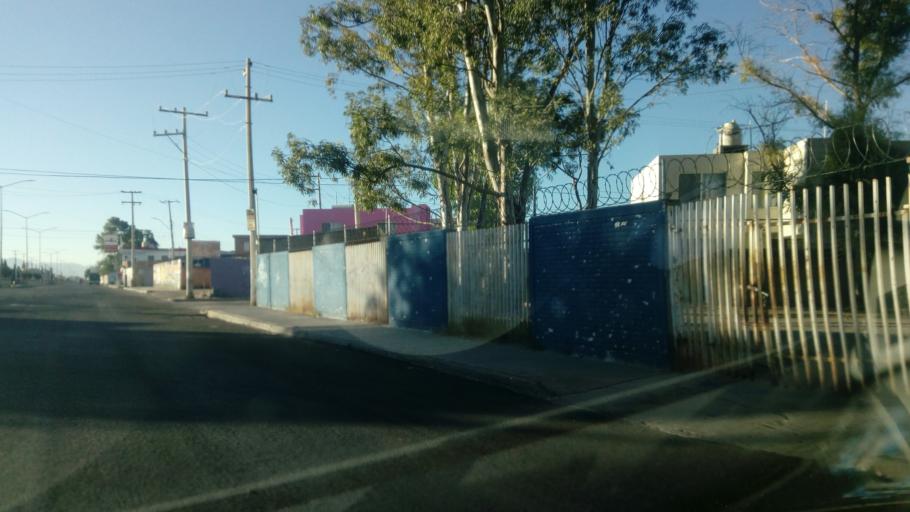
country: MX
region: Durango
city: Victoria de Durango
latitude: 24.0620
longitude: -104.5956
